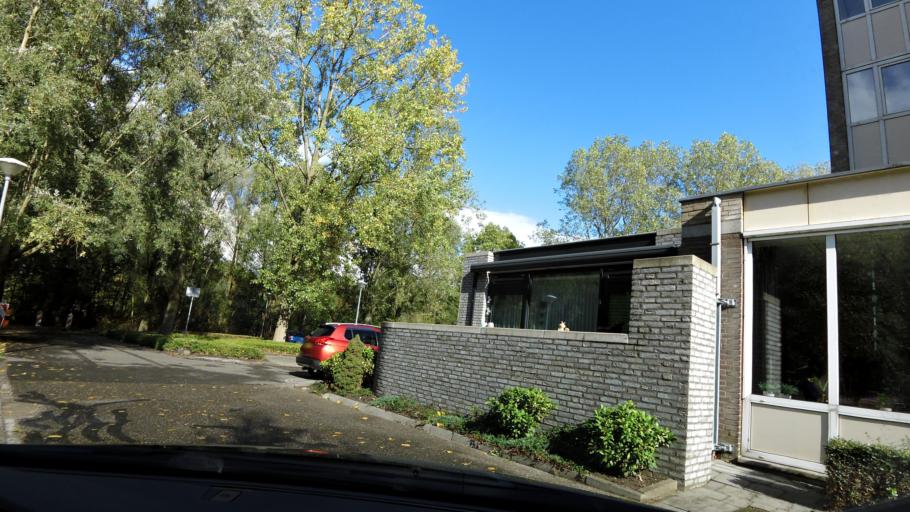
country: NL
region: Limburg
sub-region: Gemeente Brunssum
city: Brunssum
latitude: 50.9536
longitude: 5.9815
